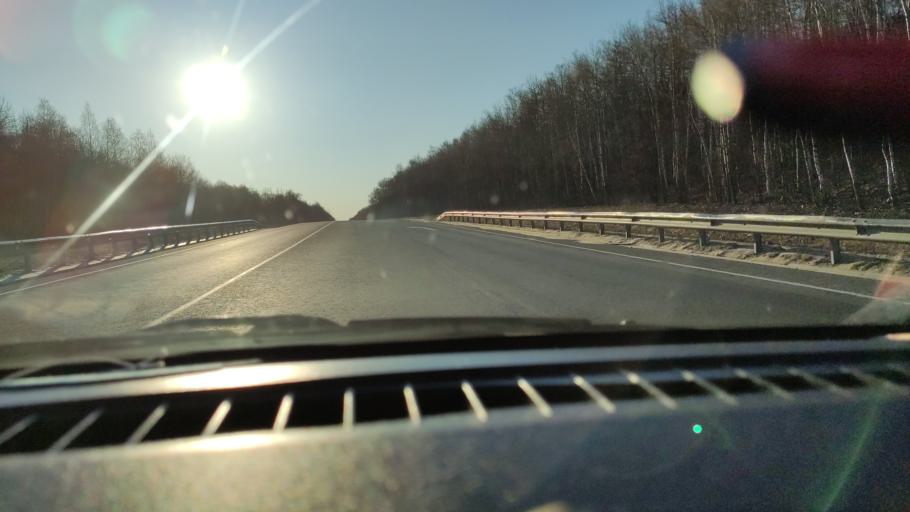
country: RU
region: Saratov
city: Vol'sk
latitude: 52.1121
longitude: 47.3254
